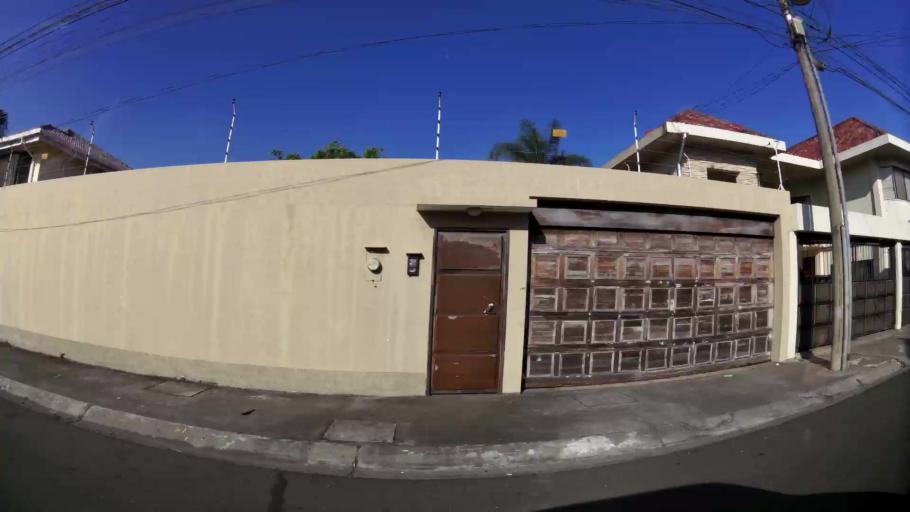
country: EC
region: Guayas
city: Santa Lucia
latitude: -2.1917
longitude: -79.9633
